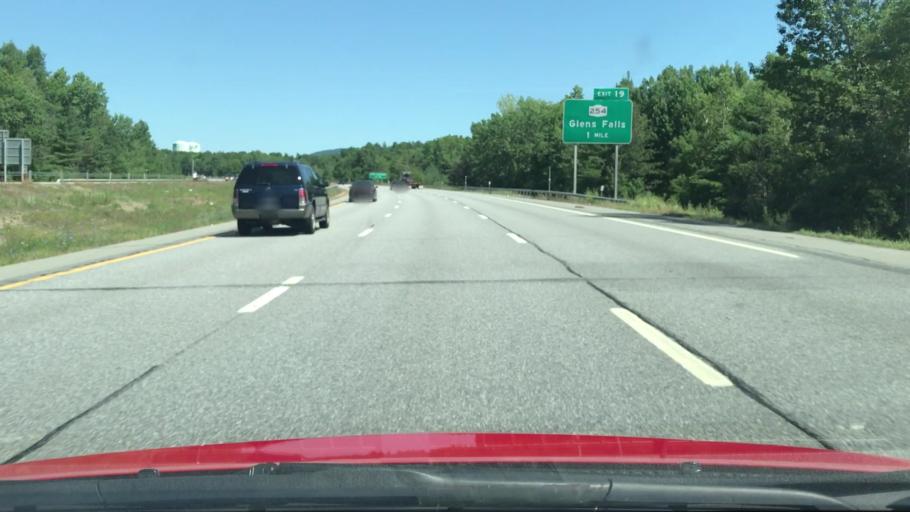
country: US
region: New York
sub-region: Warren County
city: West Glens Falls
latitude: 43.3144
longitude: -73.6747
